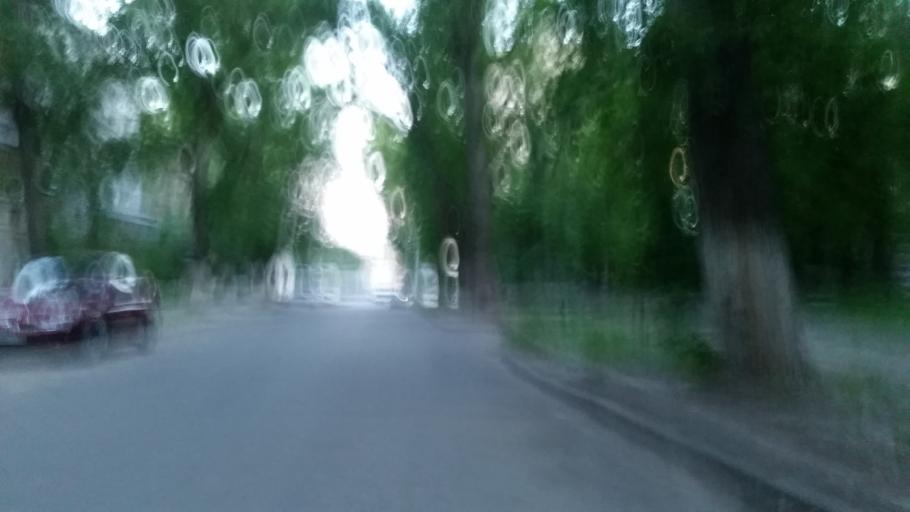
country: RU
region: Ulyanovsk
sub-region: Ulyanovskiy Rayon
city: Ulyanovsk
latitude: 54.3093
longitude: 48.3939
